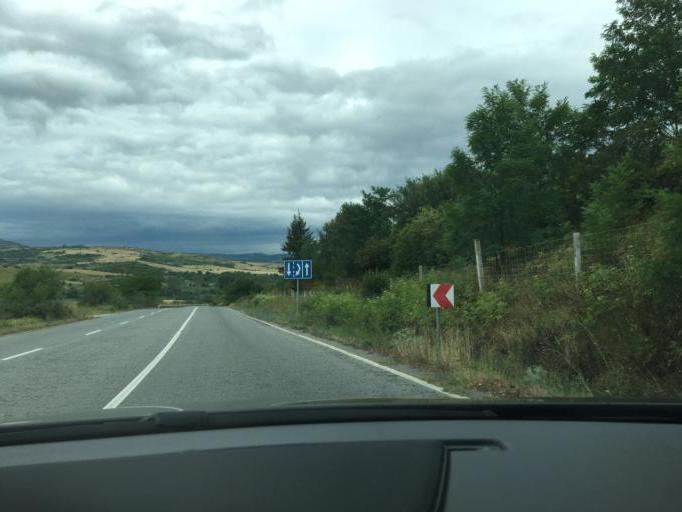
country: BG
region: Kyustendil
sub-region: Obshtina Dupnitsa
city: Dupnitsa
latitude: 42.2675
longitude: 23.0653
